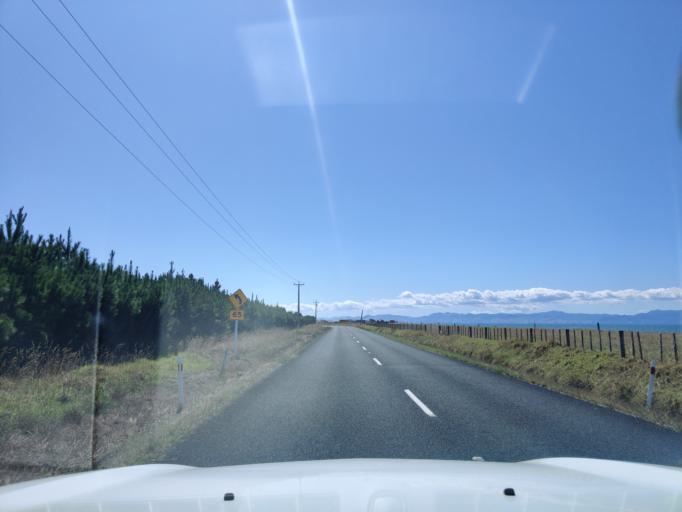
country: NZ
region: Waikato
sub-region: Thames-Coromandel District
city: Thames
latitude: -37.0660
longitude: 175.2974
